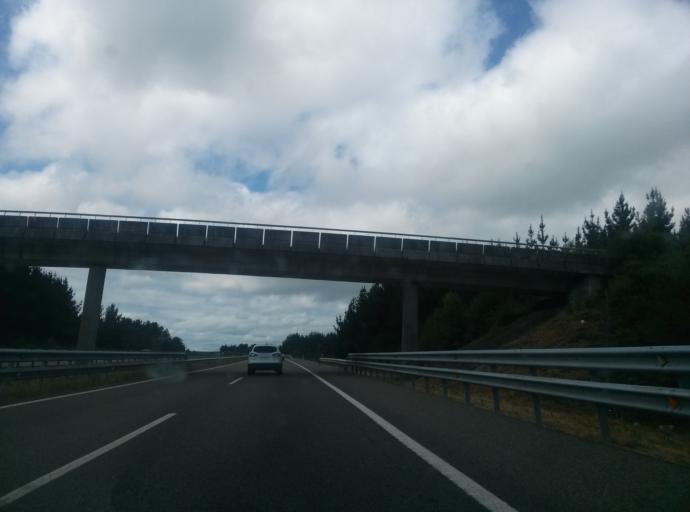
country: ES
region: Galicia
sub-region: Provincia de Lugo
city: Outeiro de Rei
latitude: 43.0874
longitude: -7.5833
